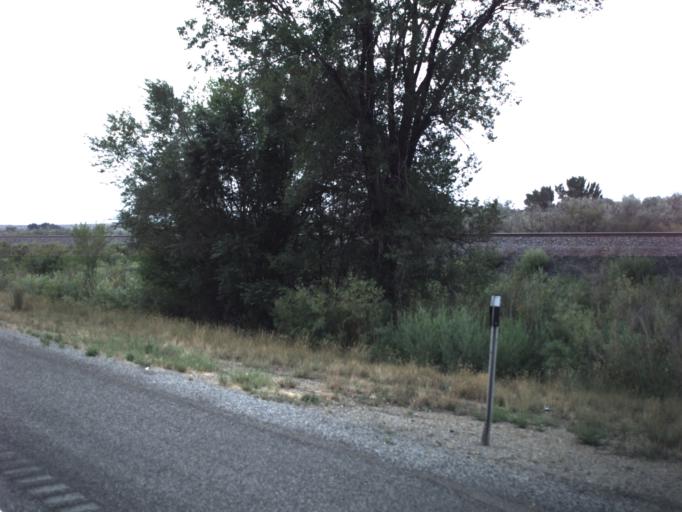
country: US
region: Utah
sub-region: Carbon County
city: Wellington
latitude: 39.5522
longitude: -110.7555
